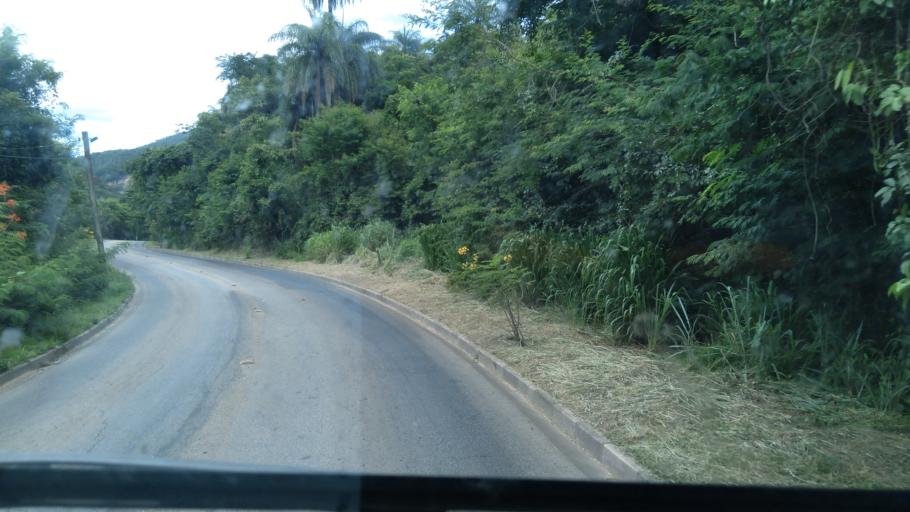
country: BR
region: Minas Gerais
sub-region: Belo Horizonte
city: Belo Horizonte
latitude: -19.8693
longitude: -43.8540
